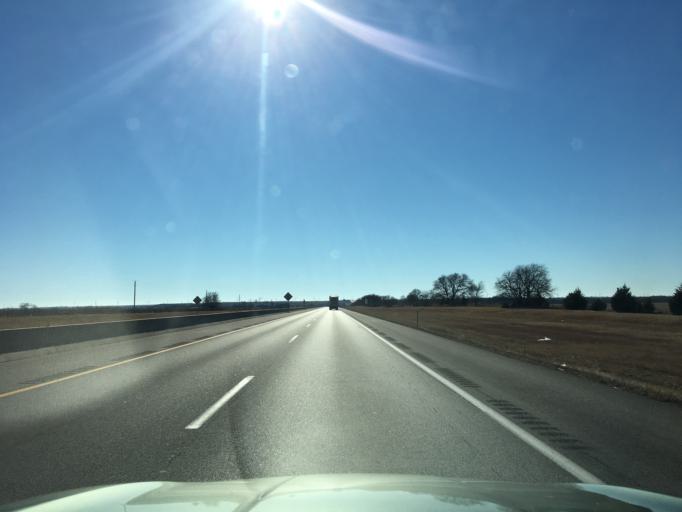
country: US
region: Kansas
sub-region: Sumner County
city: Wellington
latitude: 37.2317
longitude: -97.3389
